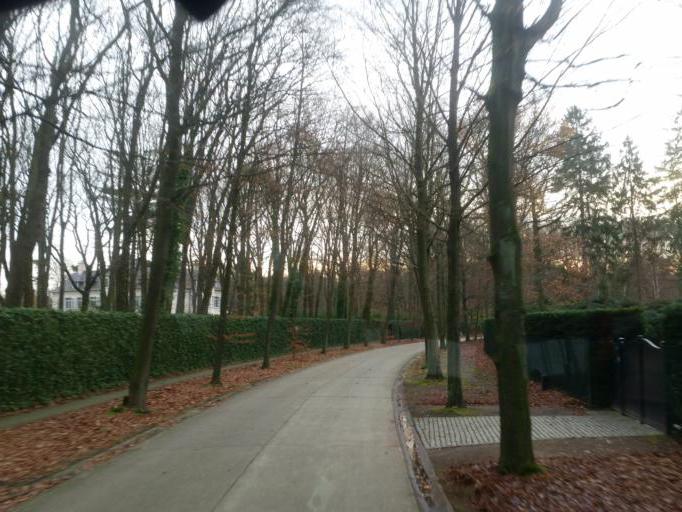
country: BE
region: Flanders
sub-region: Provincie Antwerpen
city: Brasschaat
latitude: 51.3300
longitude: 4.4893
